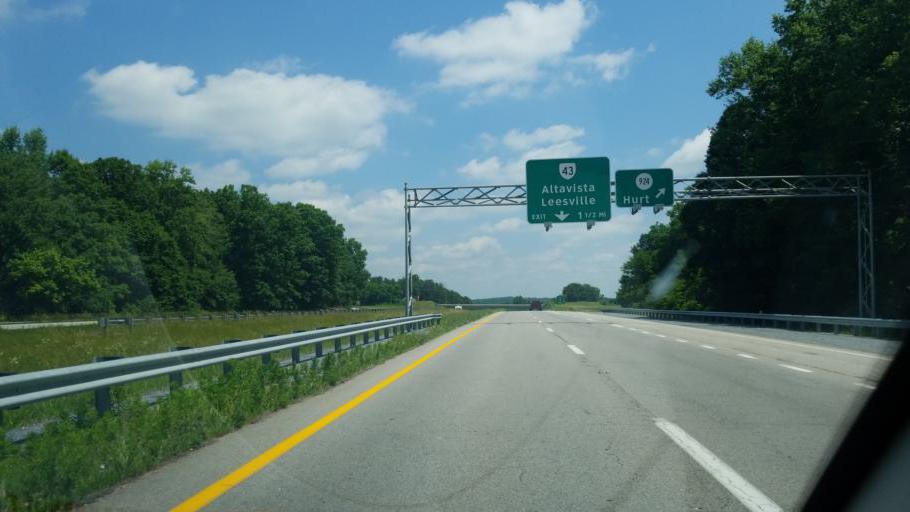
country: US
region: Virginia
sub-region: Pittsylvania County
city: Hurt
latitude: 37.1108
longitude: -79.3294
